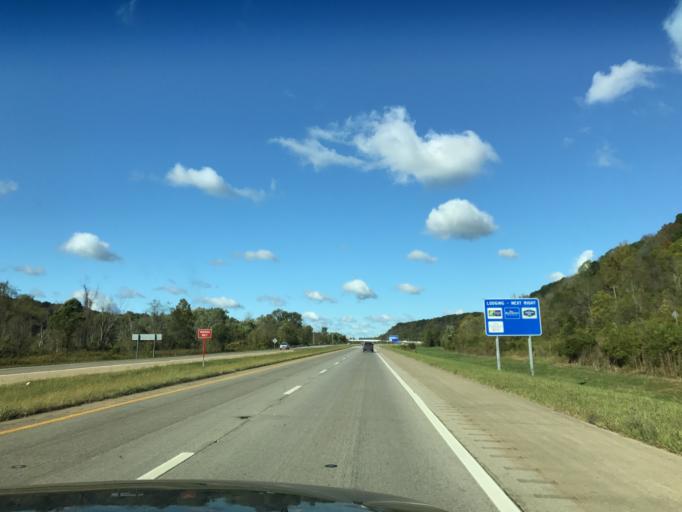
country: US
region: Ohio
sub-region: Athens County
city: Athens
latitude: 39.3343
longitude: -82.0195
